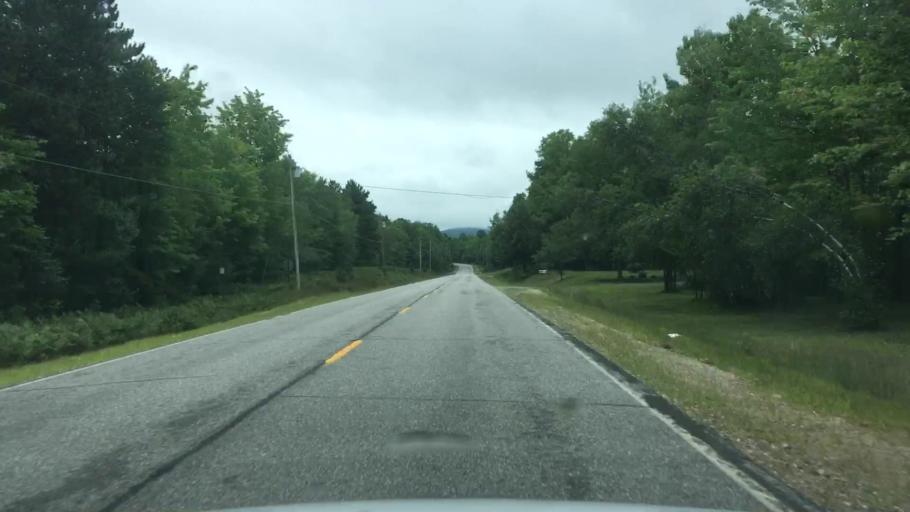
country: US
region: Maine
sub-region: Oxford County
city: Brownfield
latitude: 43.9366
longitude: -70.8852
